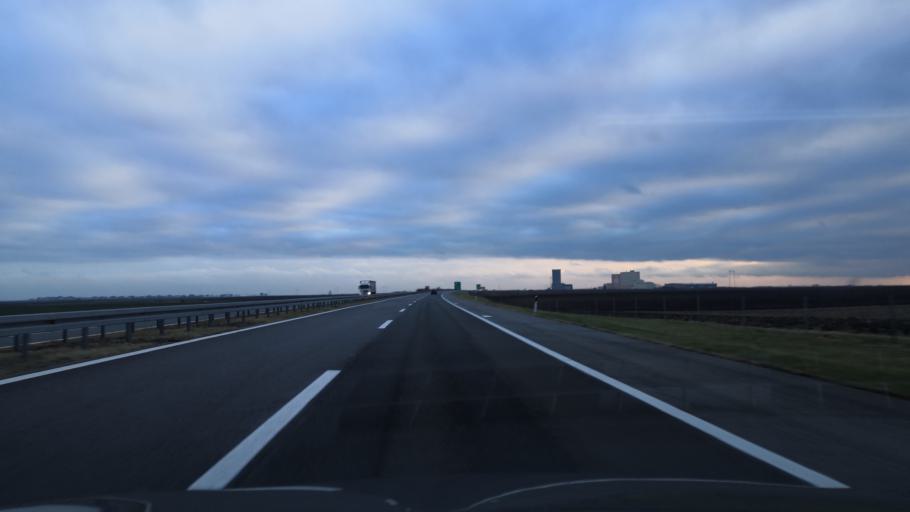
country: RS
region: Autonomna Pokrajina Vojvodina
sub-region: Severnobacki Okrug
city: Mali Igos
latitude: 45.6650
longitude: 19.7273
